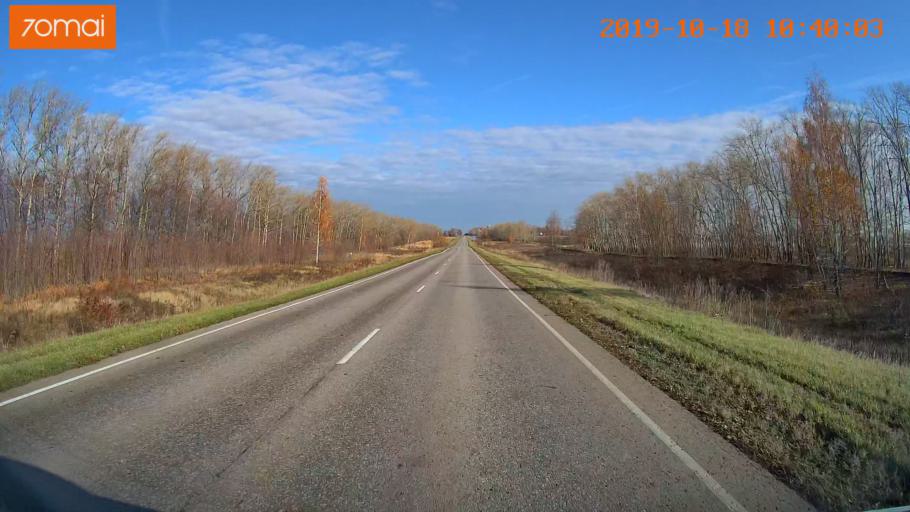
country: RU
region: Tula
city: Kurkino
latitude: 53.5954
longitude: 38.6597
